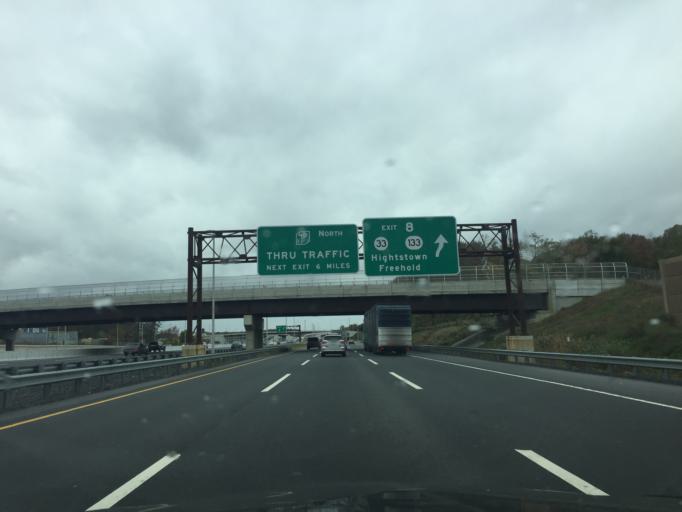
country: US
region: New Jersey
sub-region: Mercer County
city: Hightstown
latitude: 40.2568
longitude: -74.5137
